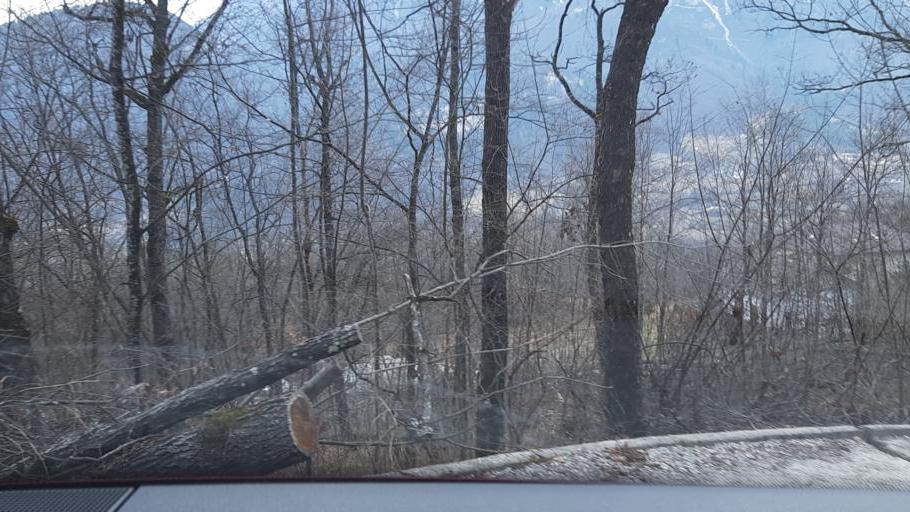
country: IT
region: Trentino-Alto Adige
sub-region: Provincia di Trento
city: Borgo
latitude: 46.0406
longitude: 11.4534
